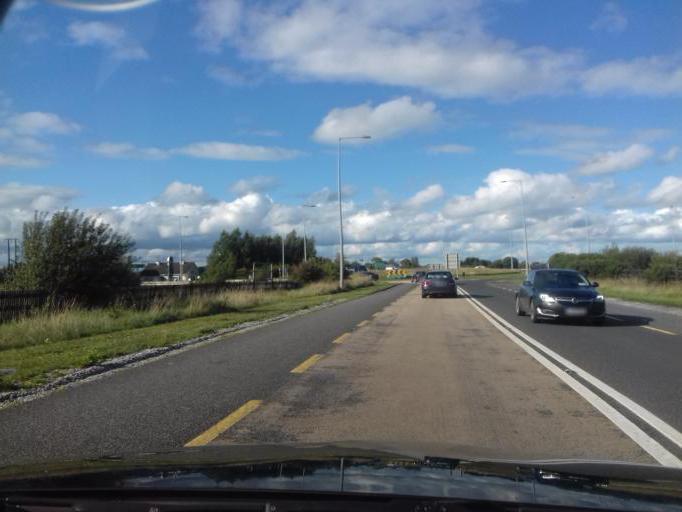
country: IE
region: Leinster
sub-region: Uibh Fhaili
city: Tullamore
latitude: 53.2759
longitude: -7.4671
